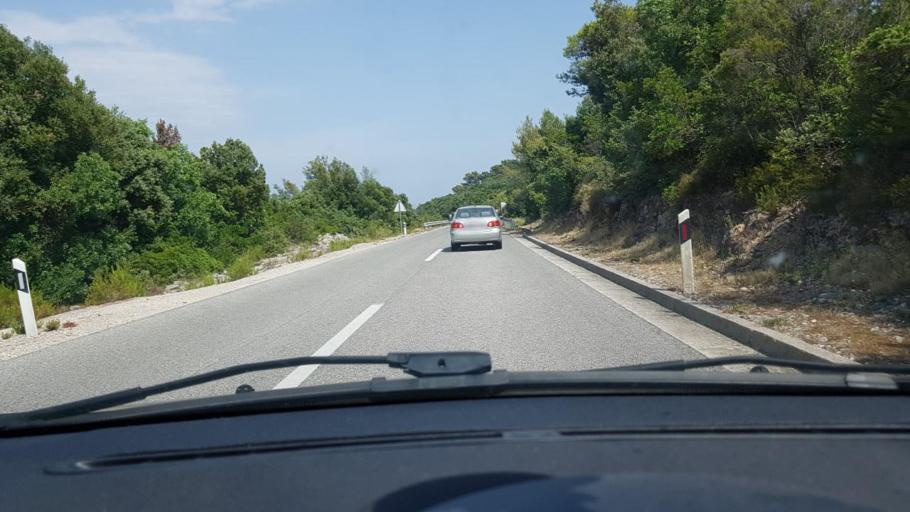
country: HR
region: Dubrovacko-Neretvanska
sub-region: Grad Korcula
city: Zrnovo
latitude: 42.9397
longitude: 17.0686
